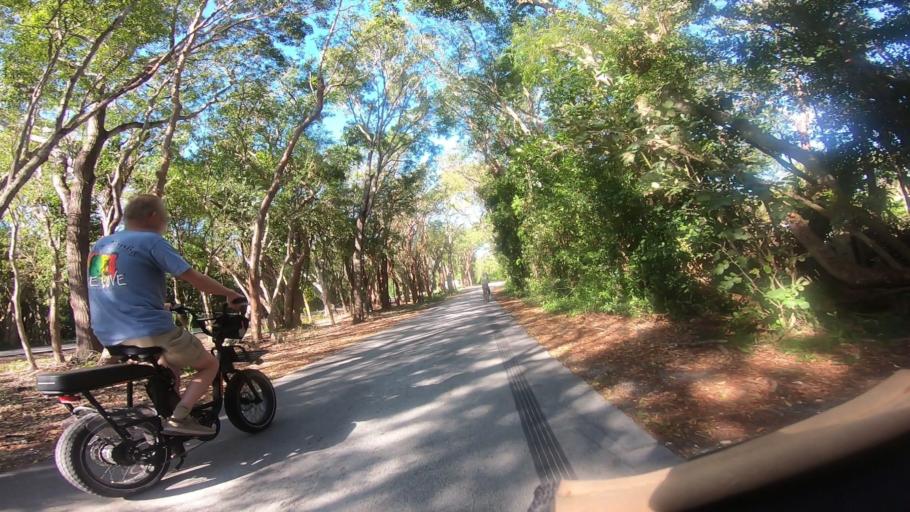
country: US
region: Florida
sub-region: Monroe County
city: Key Largo
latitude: 25.1118
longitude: -80.4250
